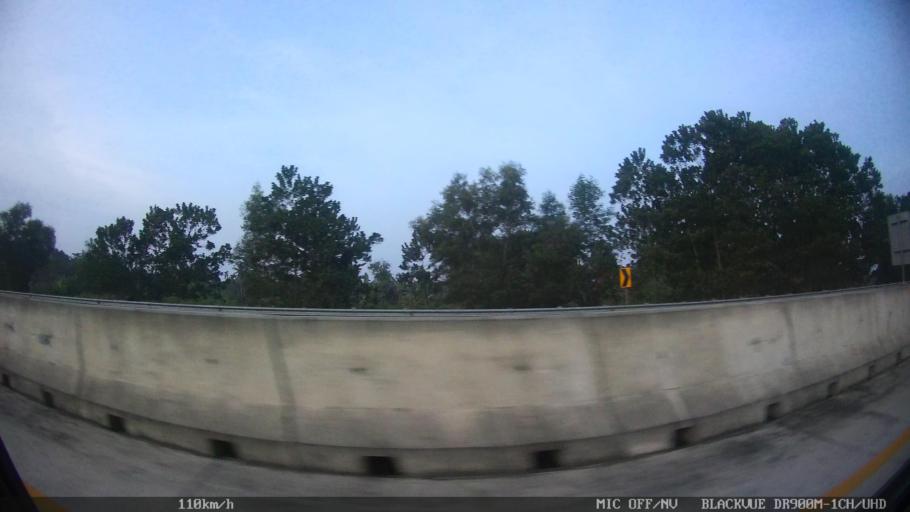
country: ID
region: Lampung
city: Pasuruan
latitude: -5.7354
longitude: 105.6880
